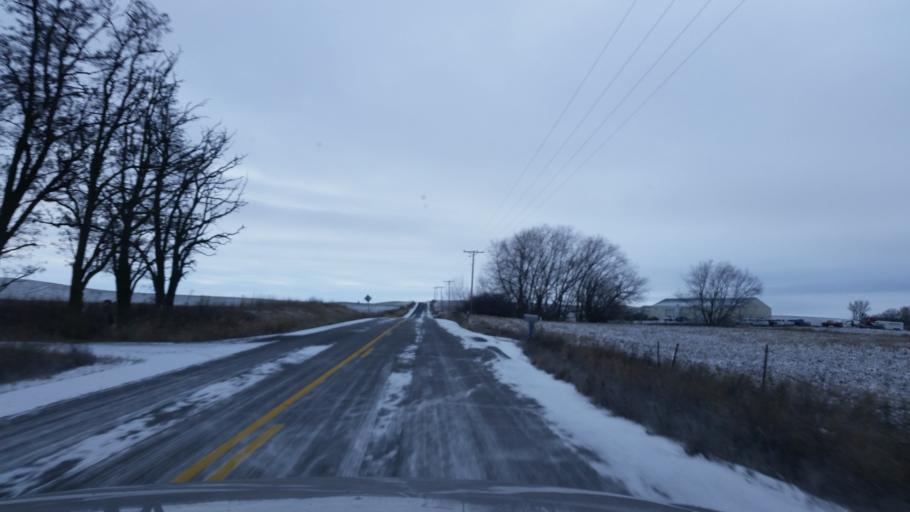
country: US
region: Washington
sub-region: Spokane County
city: Cheney
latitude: 47.3899
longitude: -117.4886
